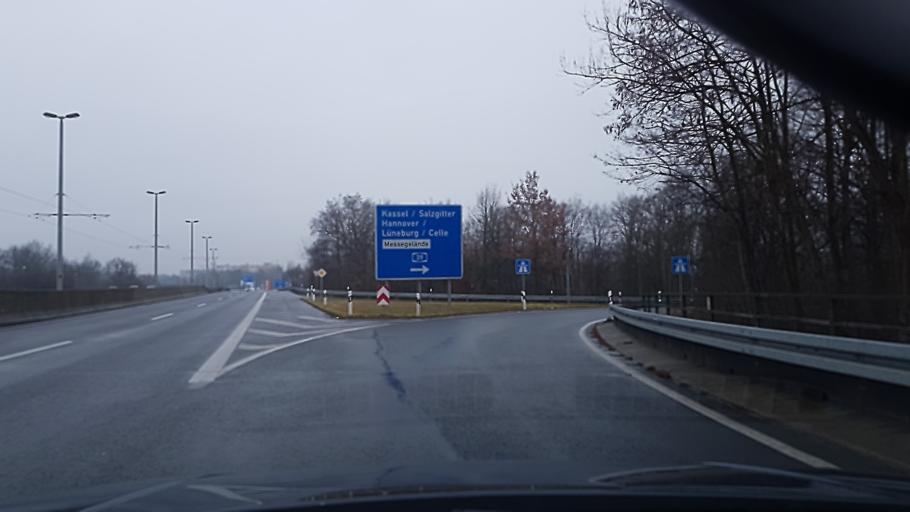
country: DE
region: Lower Saxony
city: Braunschweig
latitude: 52.2387
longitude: 10.5277
